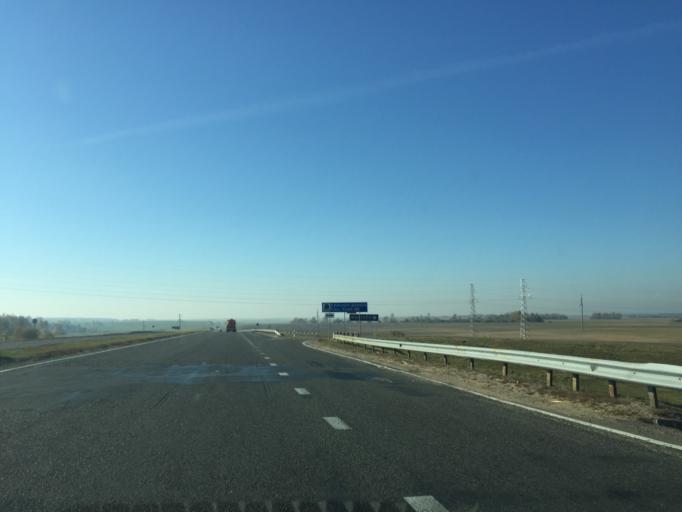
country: BY
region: Mogilev
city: Buynichy
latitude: 53.9487
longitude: 30.2228
